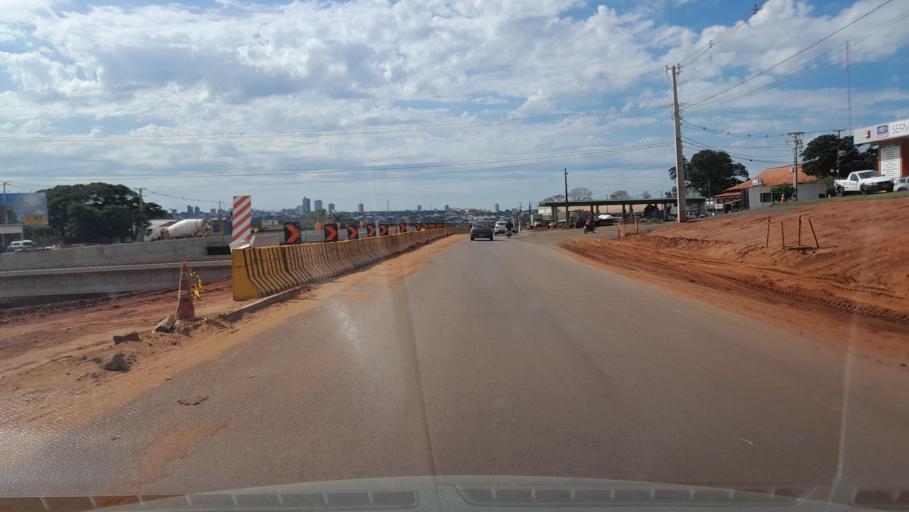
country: BR
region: Parana
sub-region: Umuarama
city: Umuarama
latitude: -23.7900
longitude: -53.3145
